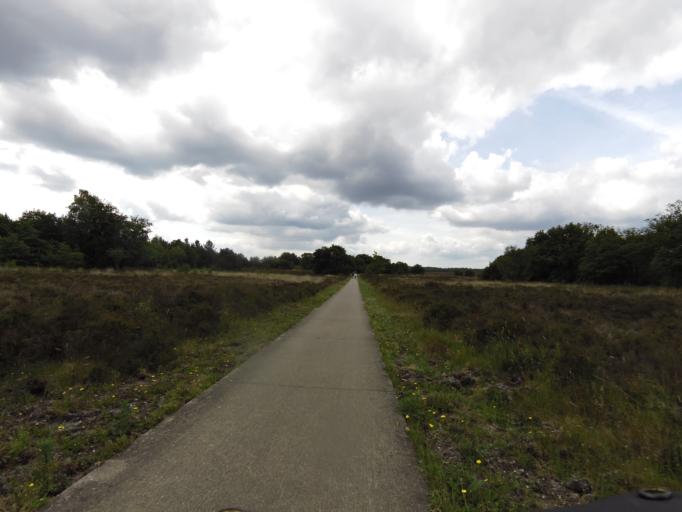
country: NL
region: Gelderland
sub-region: Gemeente Apeldoorn
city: Uddel
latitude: 52.3146
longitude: 5.8137
